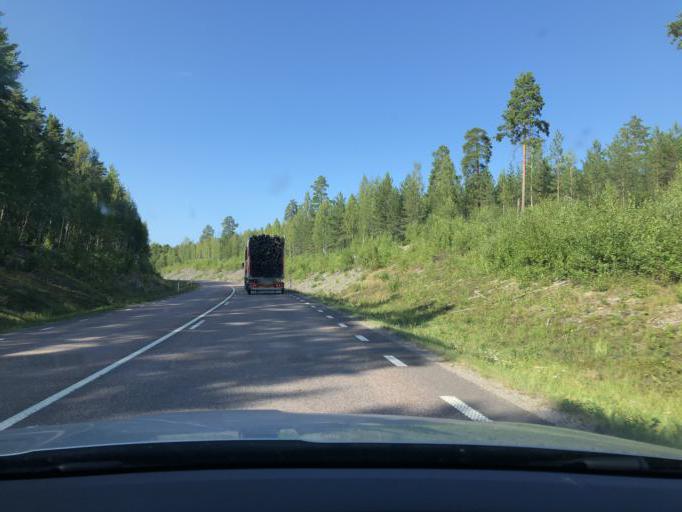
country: SE
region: Dalarna
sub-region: Faluns Kommun
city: Falun
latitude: 60.5816
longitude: 15.7742
